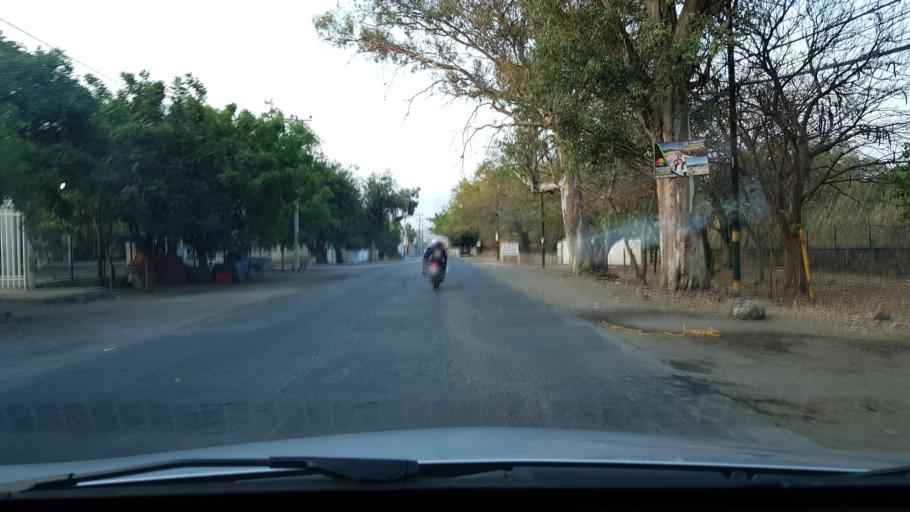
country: MX
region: Morelos
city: Jonacatepec de Leandro Valle
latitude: 18.6882
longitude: -98.8024
